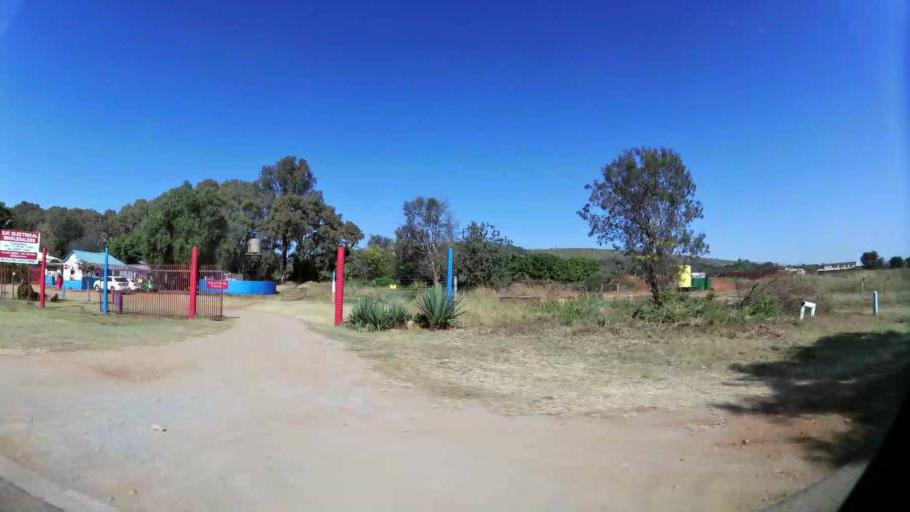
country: ZA
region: North-West
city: Ga-Rankuwa
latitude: -25.6646
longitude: 28.0684
